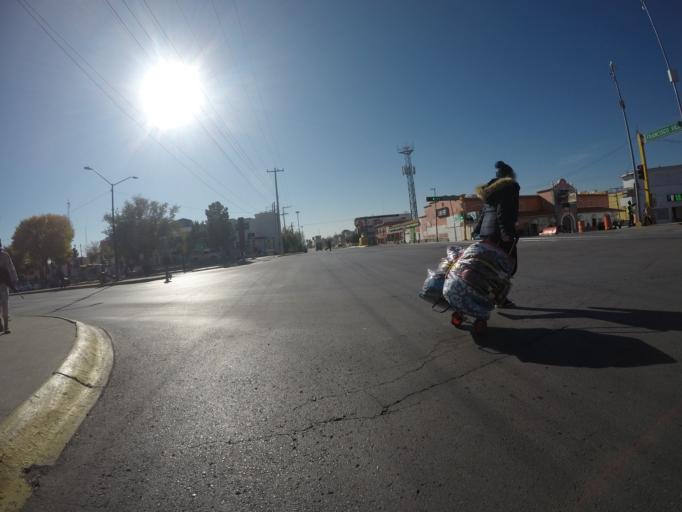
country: MX
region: Chihuahua
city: Ciudad Juarez
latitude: 31.7460
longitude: -106.4854
